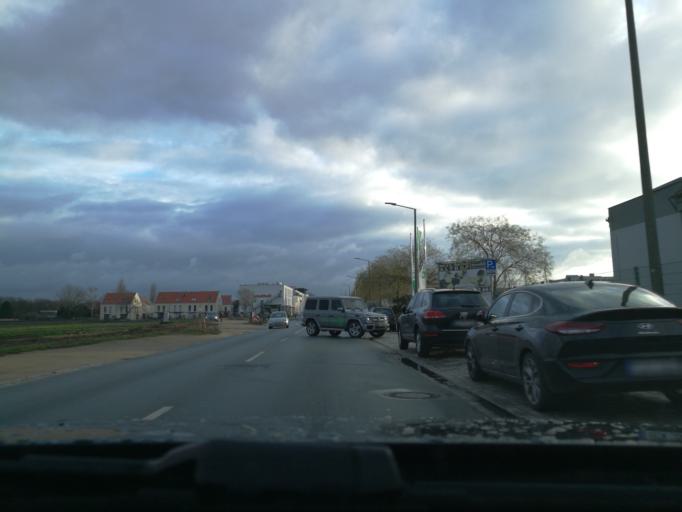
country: DE
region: Bavaria
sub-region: Regierungsbezirk Mittelfranken
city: Nuernberg
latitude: 49.4739
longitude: 11.0761
